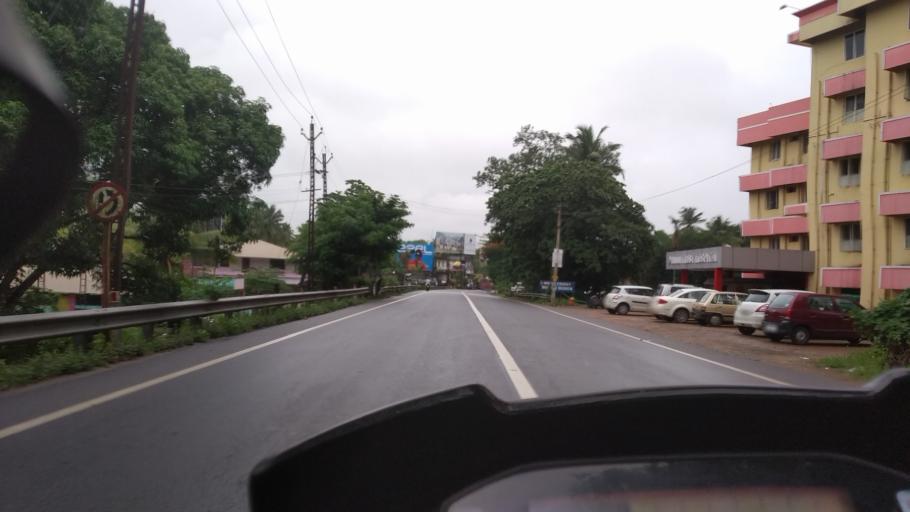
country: IN
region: Kerala
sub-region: Alappuzha
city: Mavelikara
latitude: 9.2826
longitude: 76.4428
